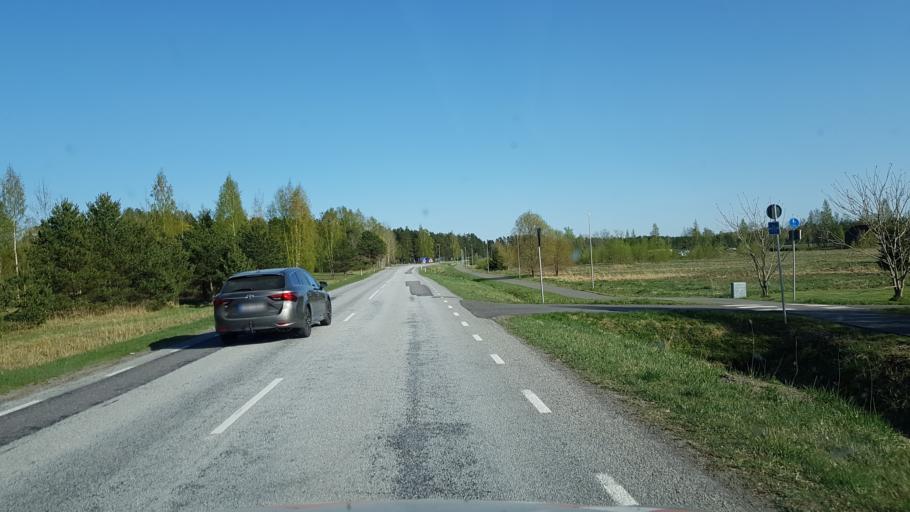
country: EE
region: Paernumaa
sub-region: Paikuse vald
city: Paikuse
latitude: 58.3599
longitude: 24.6549
